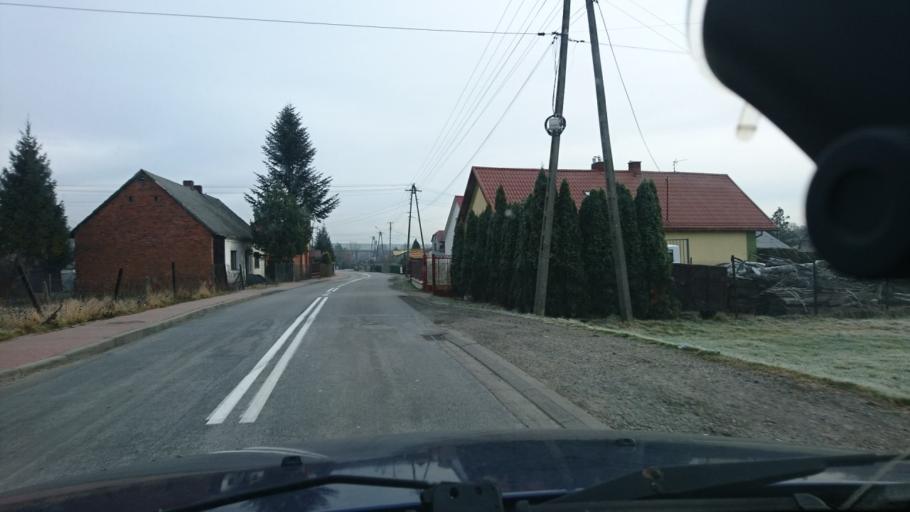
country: PL
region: Silesian Voivodeship
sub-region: Powiat bielski
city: Rybarzowice
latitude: 49.7289
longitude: 19.1113
